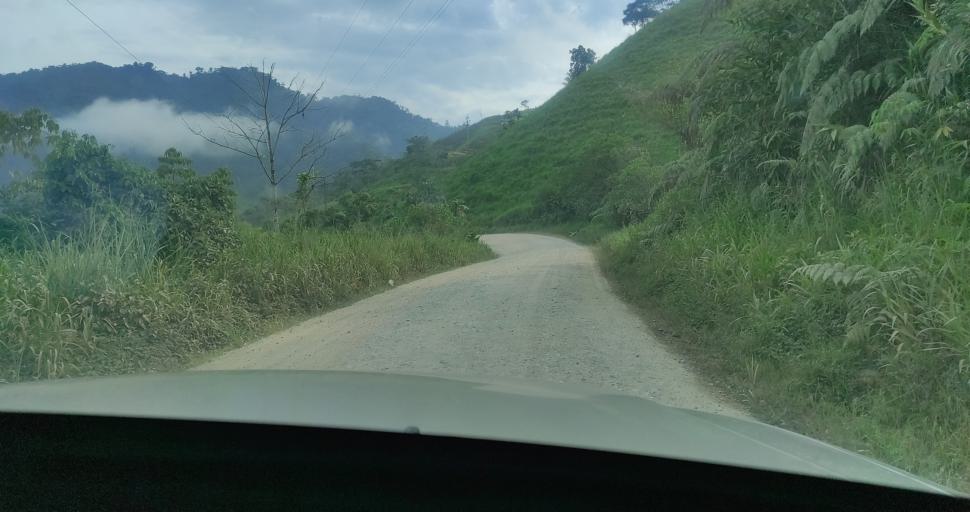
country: EC
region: Zamora-Chinchipe
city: Yantzaza
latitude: -3.7750
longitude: -78.8953
